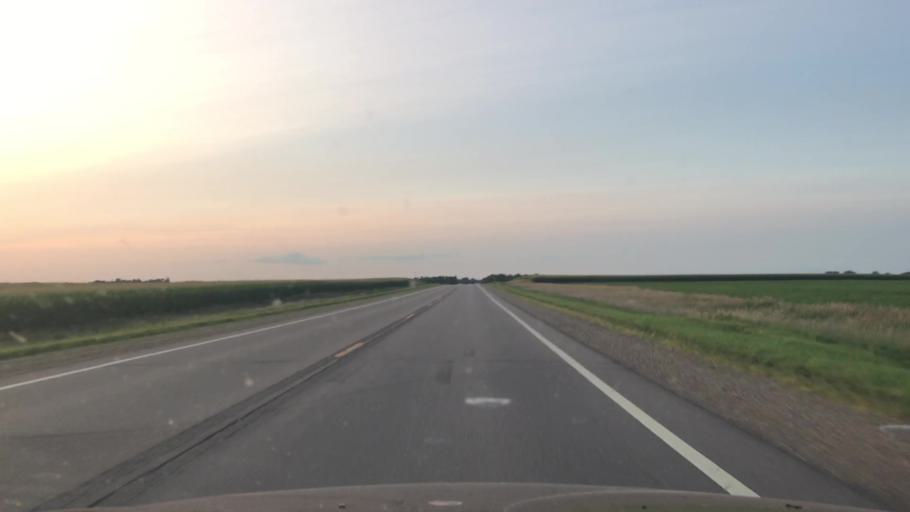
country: US
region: Minnesota
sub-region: Redwood County
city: Redwood Falls
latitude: 44.5043
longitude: -95.1178
